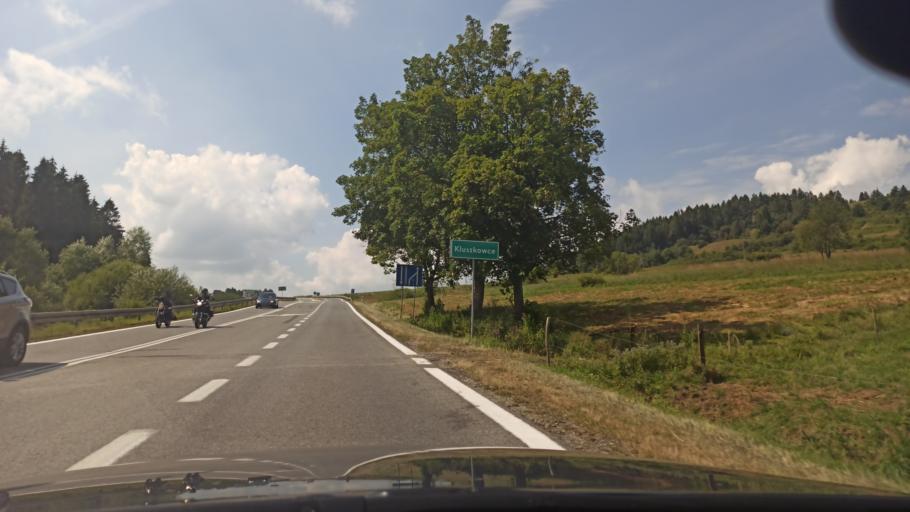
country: PL
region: Lesser Poland Voivodeship
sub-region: Powiat nowotarski
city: Krosnica
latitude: 49.4513
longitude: 20.3250
